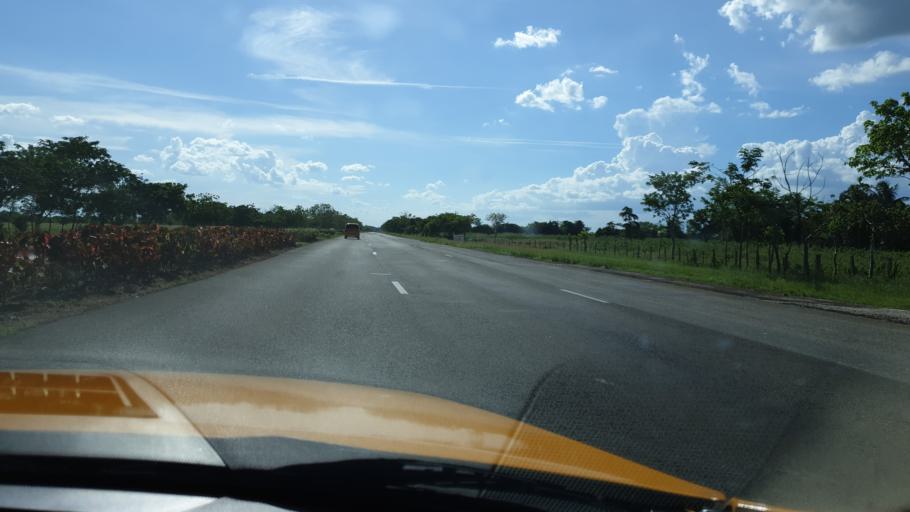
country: CU
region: Cienfuegos
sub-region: Municipio de Aguada de Pasajeros
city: Aguada de Pasajeros
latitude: 22.4101
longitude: -80.8911
